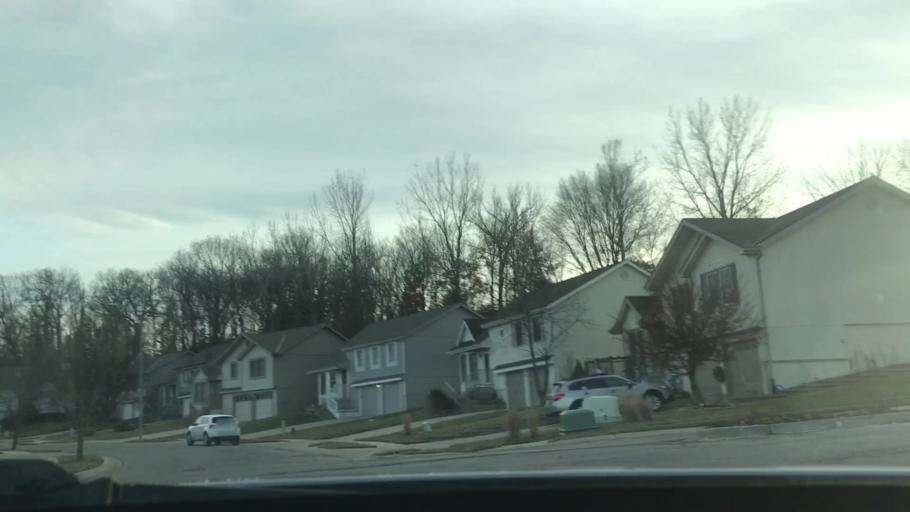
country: US
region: Missouri
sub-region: Platte County
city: Riverside
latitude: 39.2089
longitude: -94.5949
